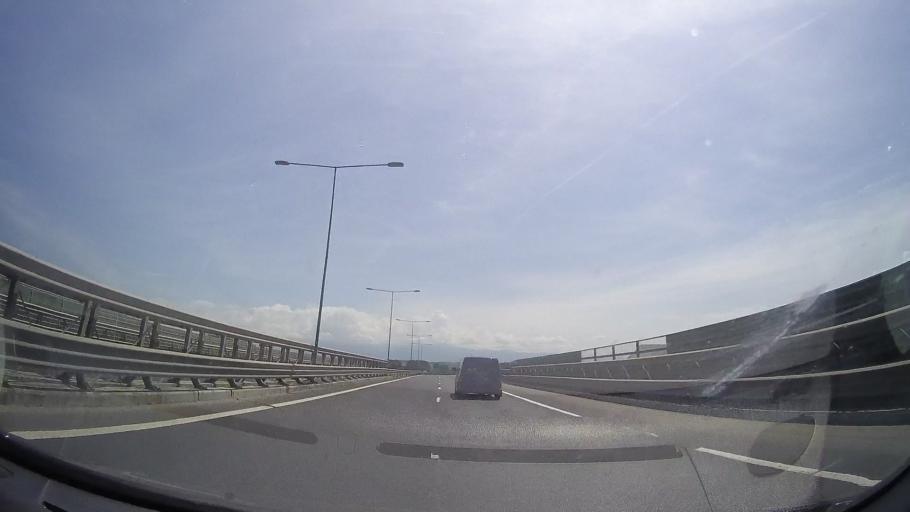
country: RO
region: Sibiu
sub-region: Municipiul Sibiu
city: Sibiu
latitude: 45.8086
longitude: 24.1746
